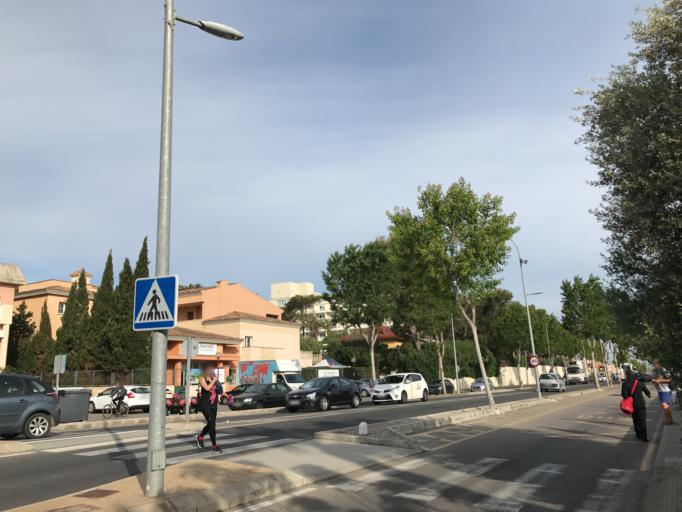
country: ES
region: Balearic Islands
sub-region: Illes Balears
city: Port d'Alcudia
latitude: 39.7655
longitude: 3.1487
